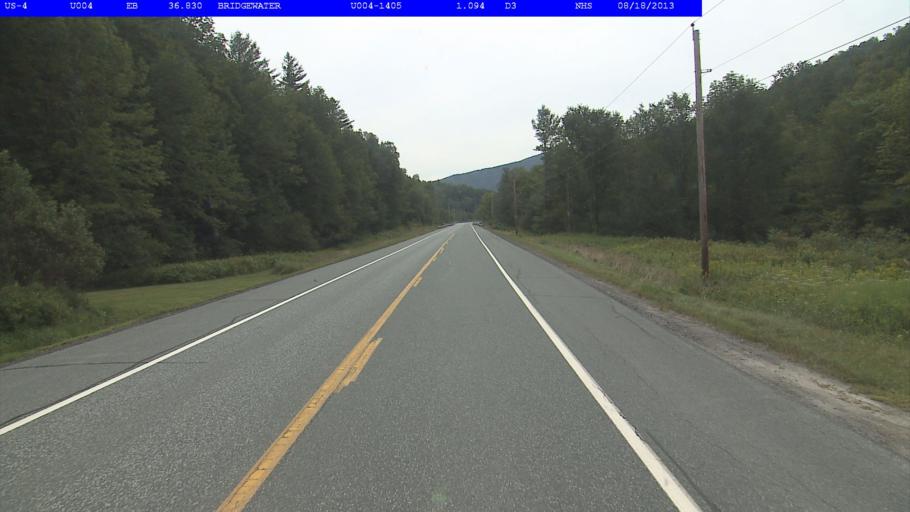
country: US
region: Vermont
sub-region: Windsor County
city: Woodstock
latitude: 43.6036
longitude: -72.7298
